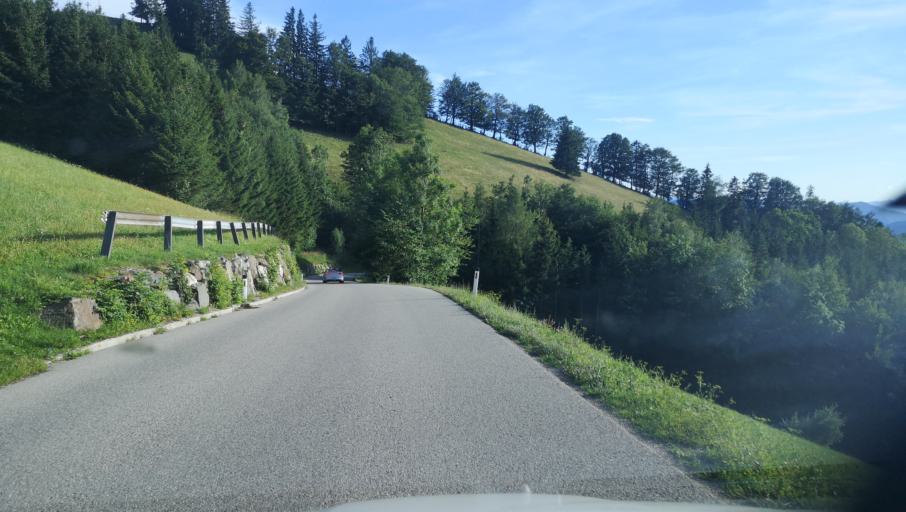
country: AT
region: Lower Austria
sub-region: Politischer Bezirk Amstetten
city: Ybbsitz
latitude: 47.9894
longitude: 14.8529
